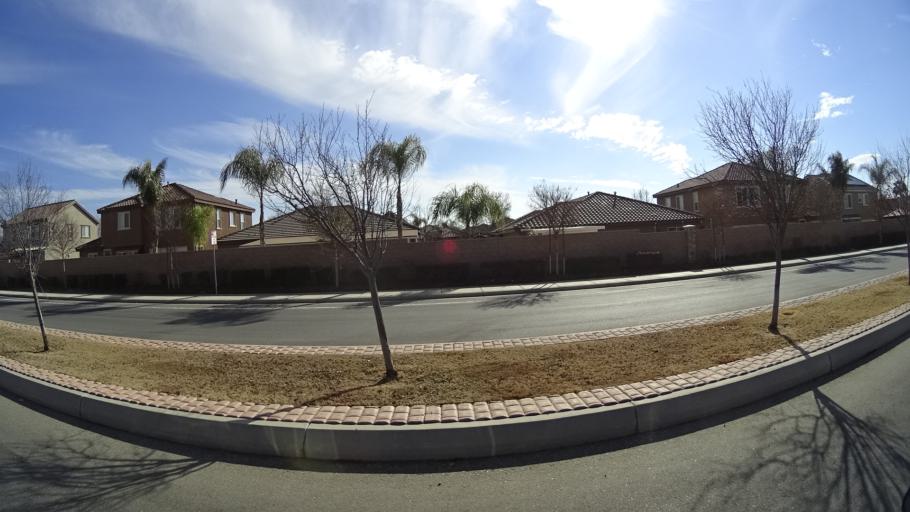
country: US
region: California
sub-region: Kern County
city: Oildale
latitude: 35.4070
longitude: -118.8933
